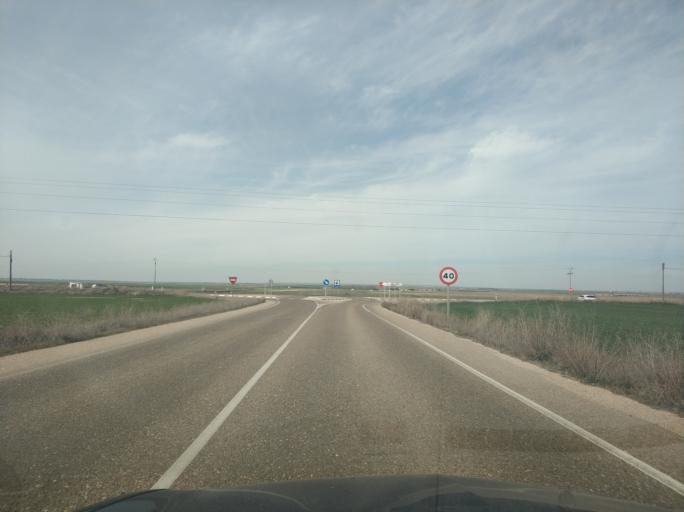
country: ES
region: Castille and Leon
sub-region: Provincia de Salamanca
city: Castellanos de Moriscos
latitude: 41.0314
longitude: -5.5782
